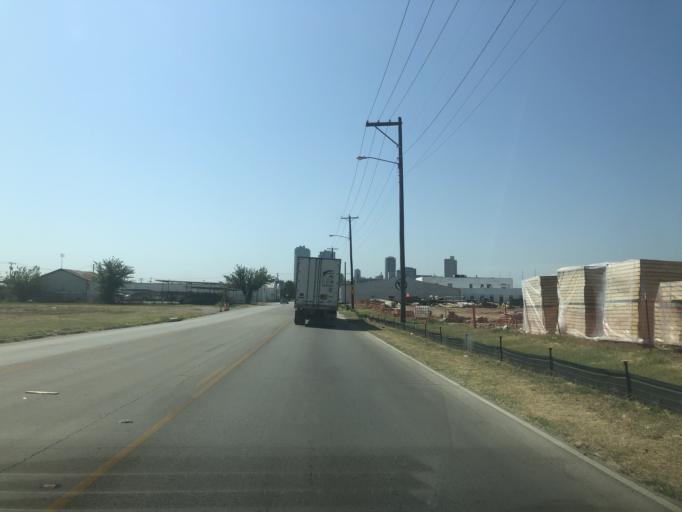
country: US
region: Texas
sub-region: Tarrant County
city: Fort Worth
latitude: 32.7715
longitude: -97.3416
